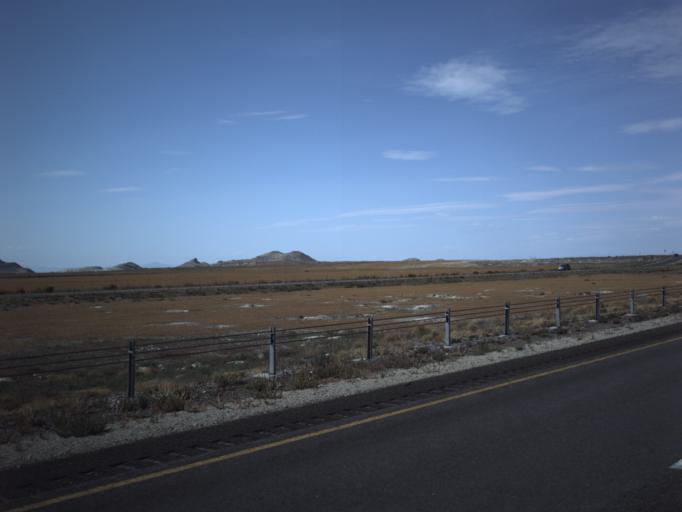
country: US
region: Utah
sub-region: Tooele County
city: Wendover
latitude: 40.7273
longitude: -113.2515
